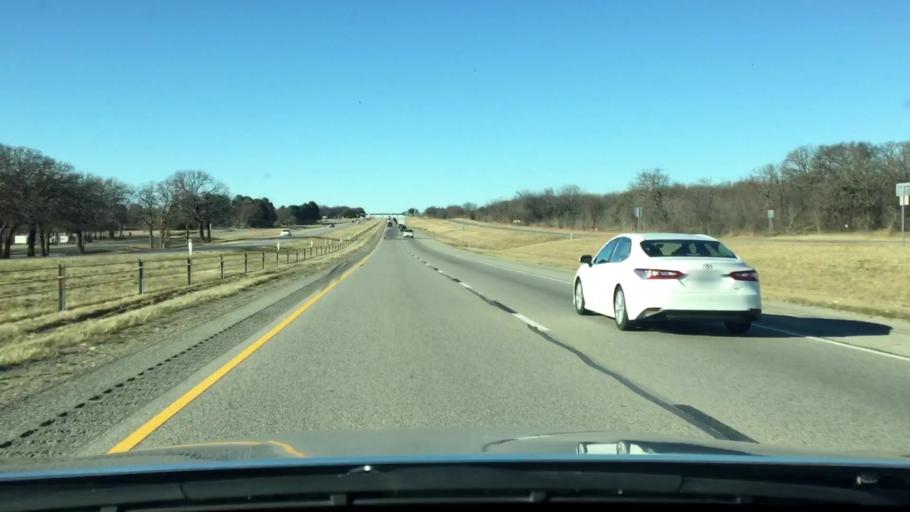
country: US
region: Texas
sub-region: Johnson County
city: Alvarado
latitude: 32.3702
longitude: -97.2021
